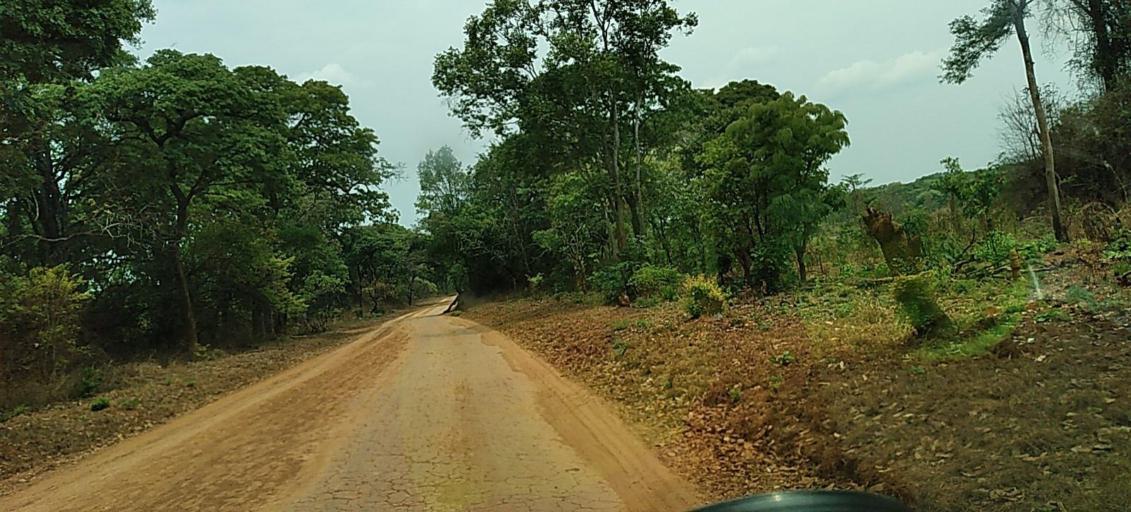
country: ZM
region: North-Western
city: Solwezi
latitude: -12.8206
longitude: 26.5366
